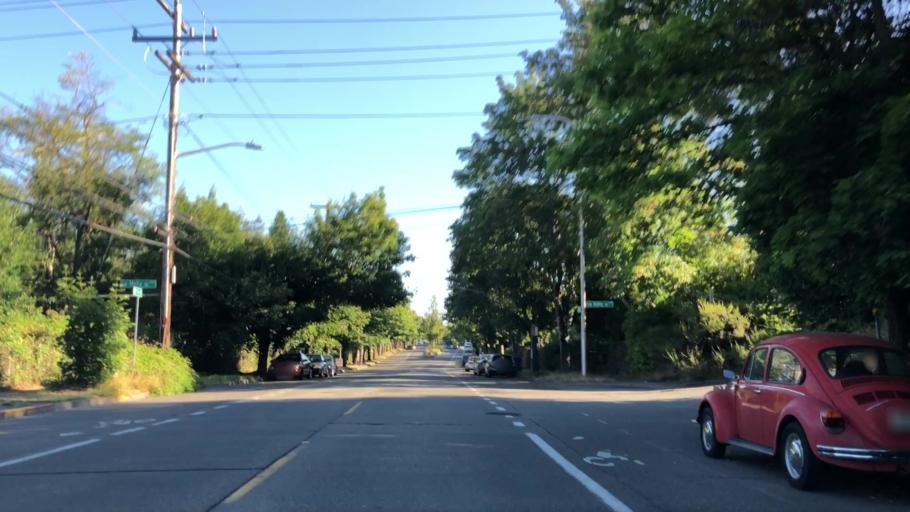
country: US
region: Washington
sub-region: King County
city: White Center
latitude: 47.5427
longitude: -122.3550
